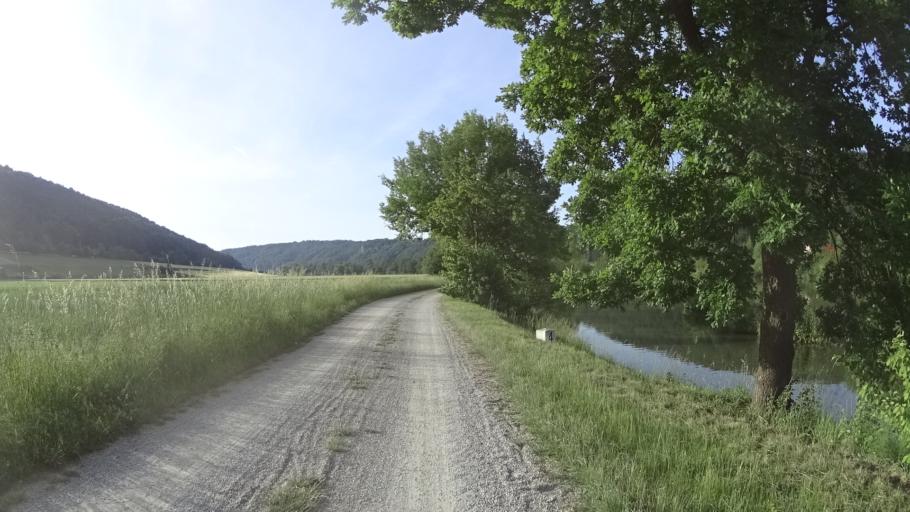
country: DE
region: Bavaria
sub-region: Lower Bavaria
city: Riedenburg
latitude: 48.9848
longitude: 11.6337
